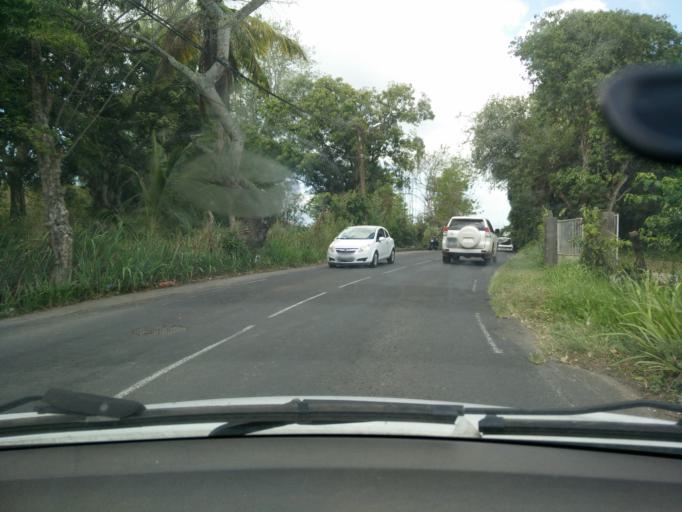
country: GP
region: Guadeloupe
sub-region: Guadeloupe
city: Les Abymes
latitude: 16.2611
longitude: -61.5049
